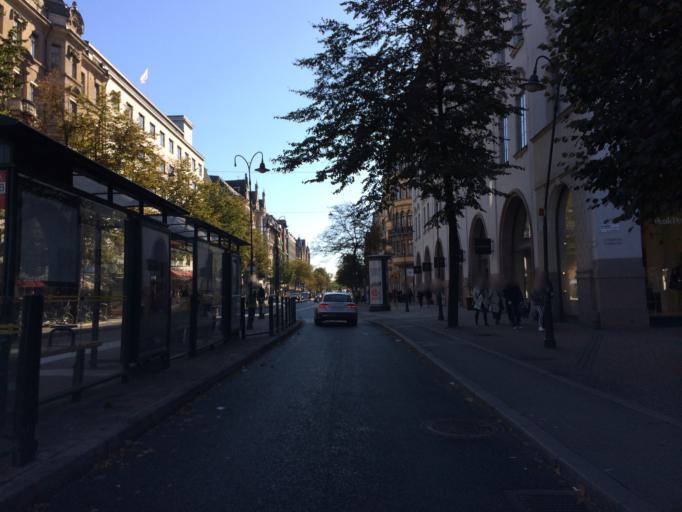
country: SE
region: Stockholm
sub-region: Stockholms Kommun
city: Stockholm
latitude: 59.3357
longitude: 18.0728
